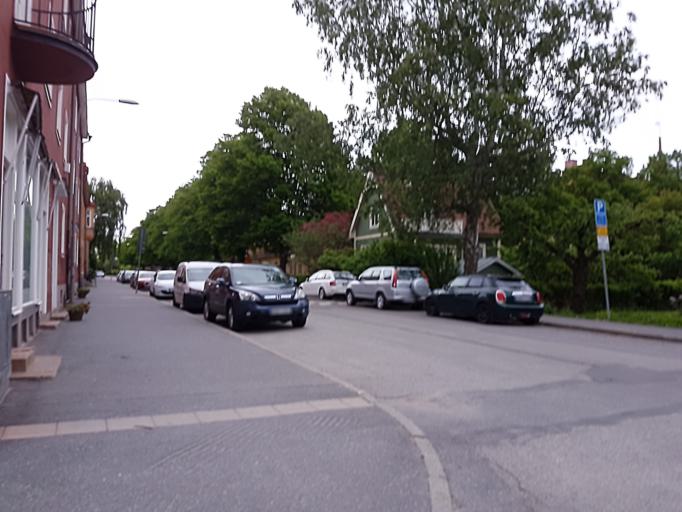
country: SE
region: Stockholm
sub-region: Stockholms Kommun
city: Arsta
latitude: 59.2835
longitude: 18.0831
